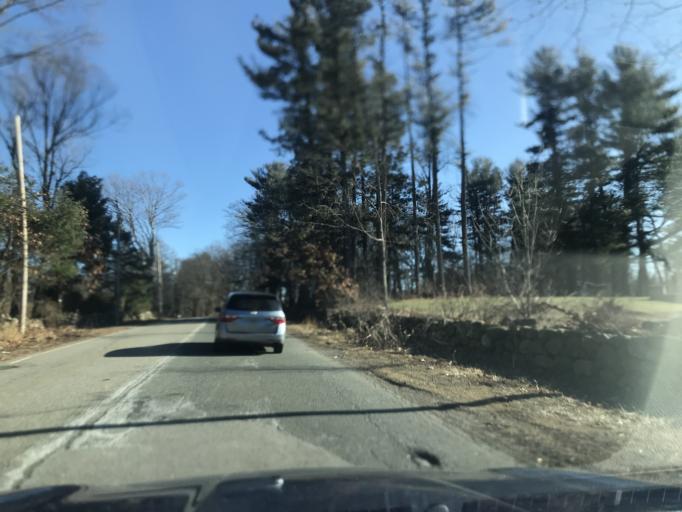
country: US
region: Massachusetts
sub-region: Essex County
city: North Andover
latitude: 42.7134
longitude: -71.0958
